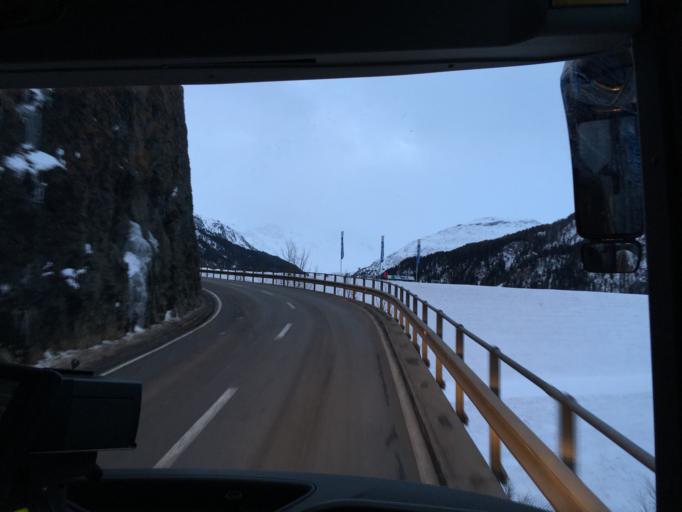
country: CH
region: Grisons
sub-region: Albula District
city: Tiefencastel
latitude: 46.5112
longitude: 9.6334
